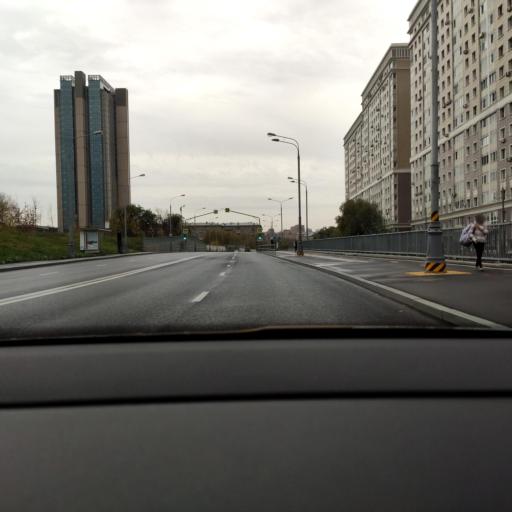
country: RU
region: Moscow
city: Ramenki
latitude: 55.6892
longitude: 37.5182
